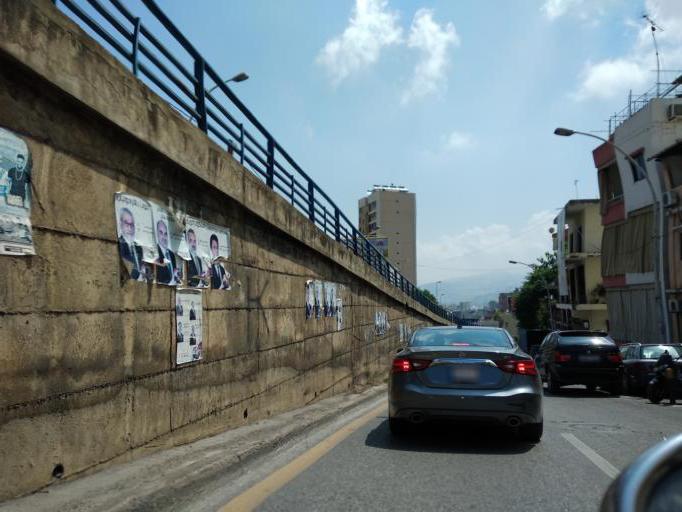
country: LB
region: Beyrouth
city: Beirut
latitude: 33.8895
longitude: 35.5277
